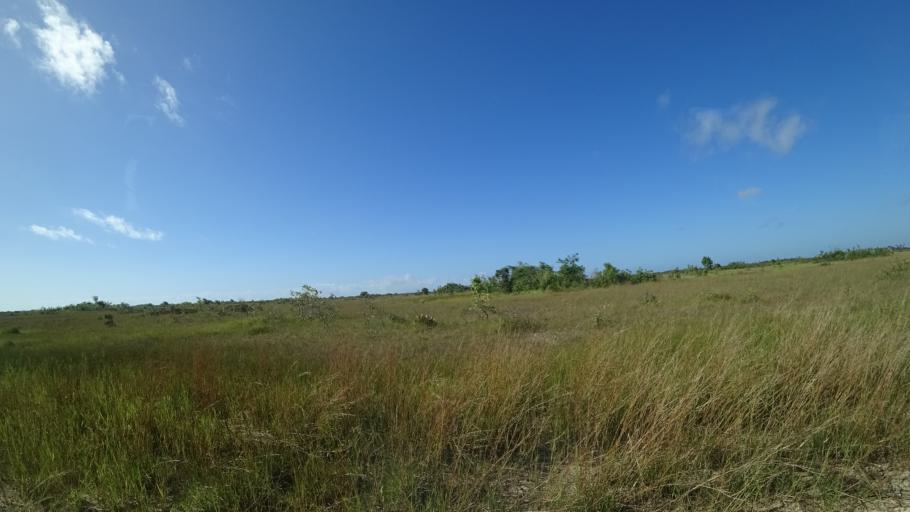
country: MZ
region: Sofala
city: Beira
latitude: -19.7004
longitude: 35.0269
